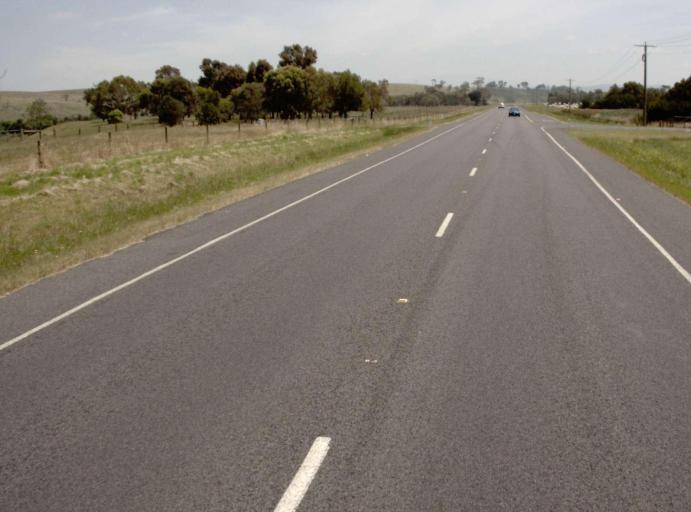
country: AU
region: Victoria
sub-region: Latrobe
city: Traralgon
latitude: -38.2394
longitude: 146.5438
